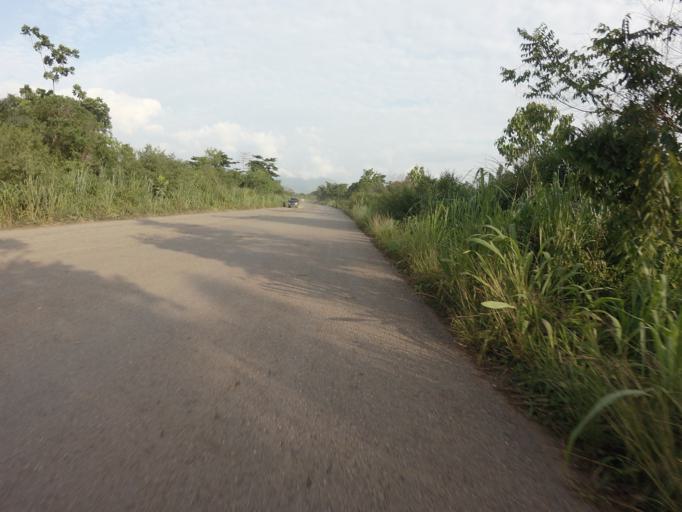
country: GH
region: Volta
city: Kpandu
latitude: 6.9787
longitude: 0.4486
